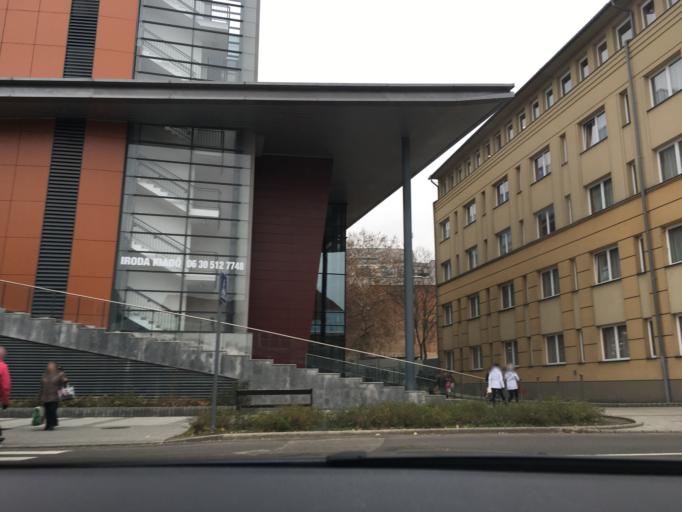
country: HU
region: Hajdu-Bihar
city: Debrecen
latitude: 47.5322
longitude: 21.6270
